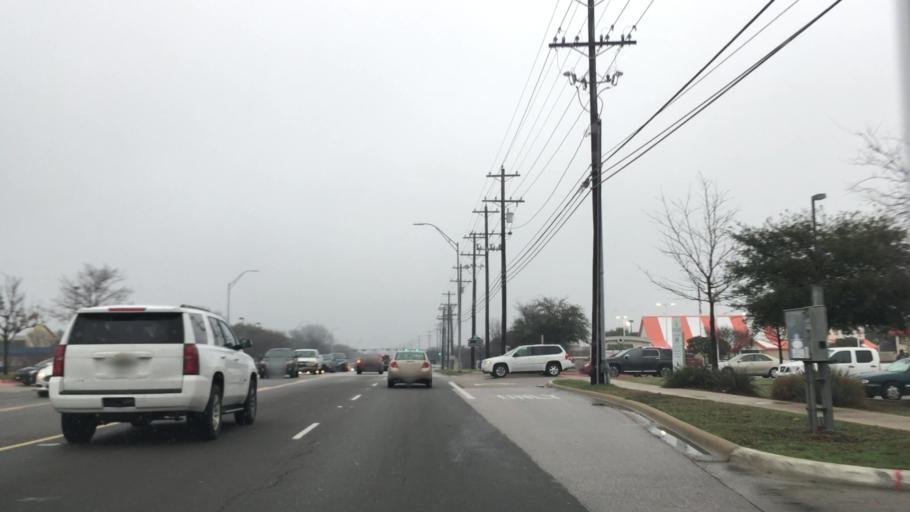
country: US
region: Texas
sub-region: Williamson County
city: Cedar Park
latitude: 30.4791
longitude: -97.8337
